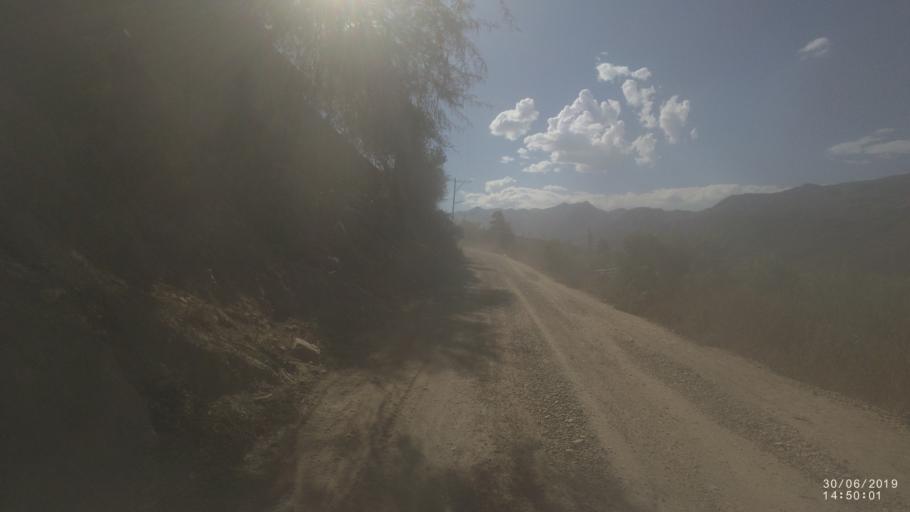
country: BO
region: Cochabamba
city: Irpa Irpa
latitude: -17.7798
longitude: -66.3425
